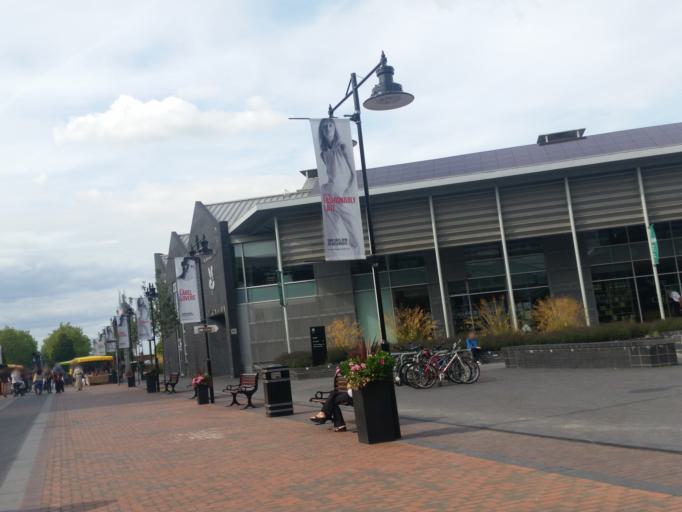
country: GB
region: England
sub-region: Borough of Swindon
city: Swindon
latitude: 51.5634
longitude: -1.7977
